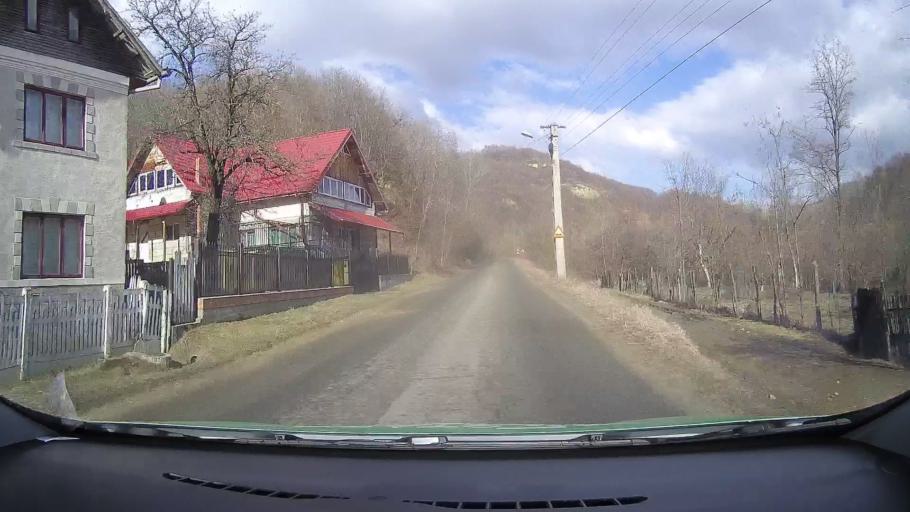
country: RO
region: Dambovita
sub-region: Oras Pucioasa
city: Pucioasa
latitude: 45.0997
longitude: 25.4426
